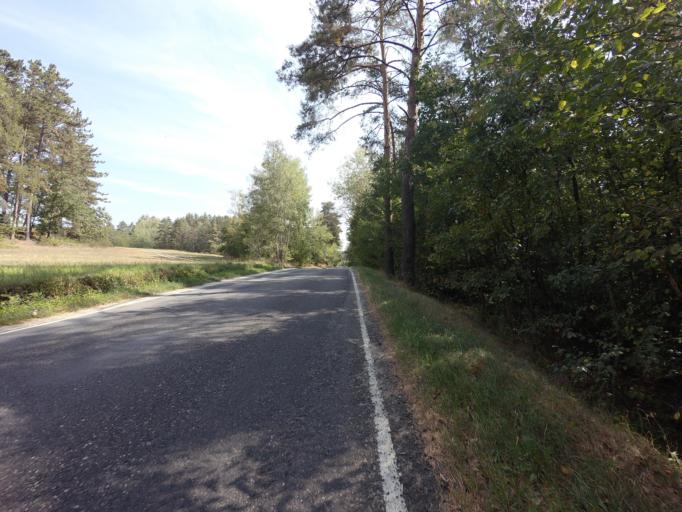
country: CZ
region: Central Bohemia
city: Petrovice
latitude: 49.5667
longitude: 14.3638
